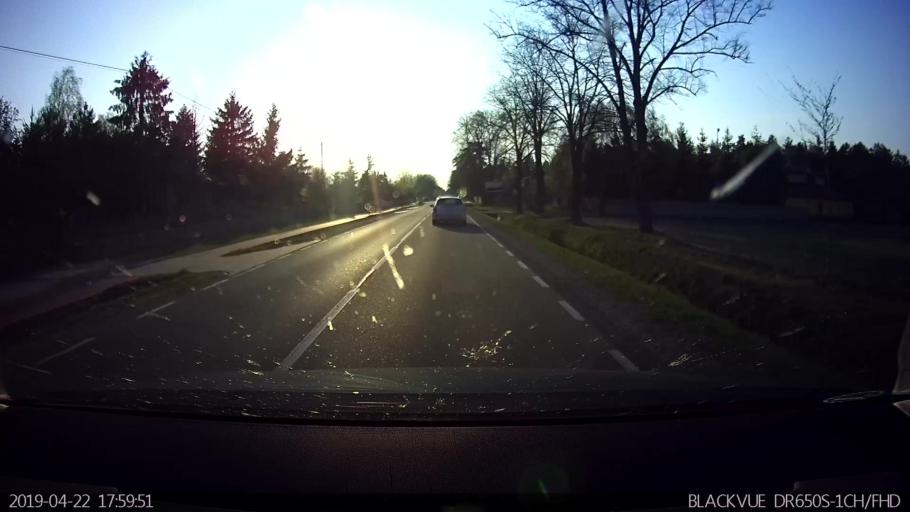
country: PL
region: Masovian Voivodeship
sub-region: Powiat wegrowski
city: Korytnica
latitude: 52.4750
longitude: 21.8556
